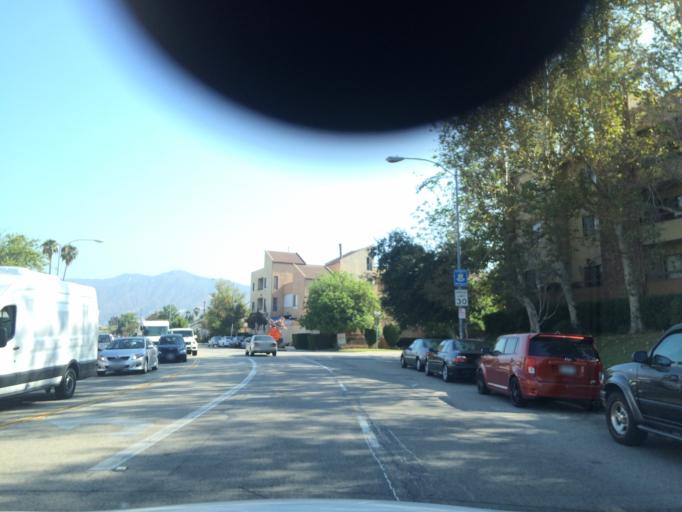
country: US
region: California
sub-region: Los Angeles County
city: Glendale
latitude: 34.1430
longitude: -118.2642
